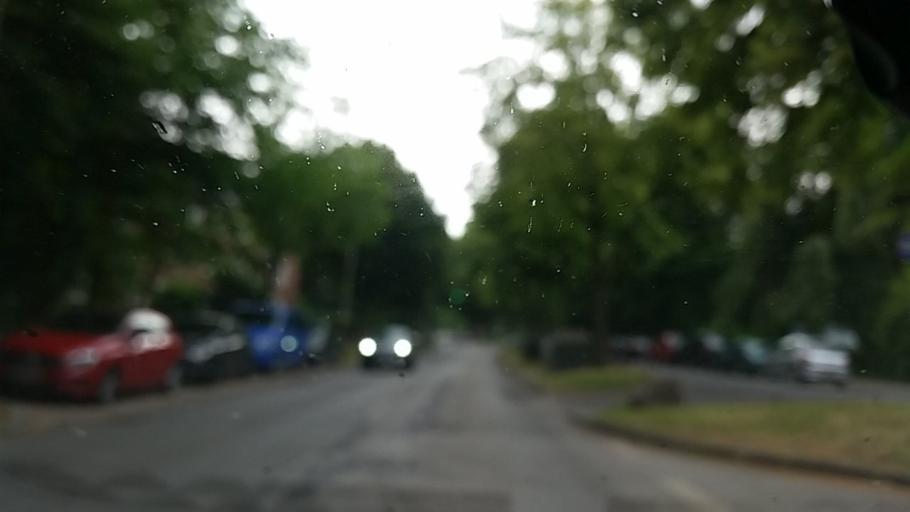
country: DE
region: Hamburg
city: Altona
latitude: 53.5624
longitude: 9.9054
